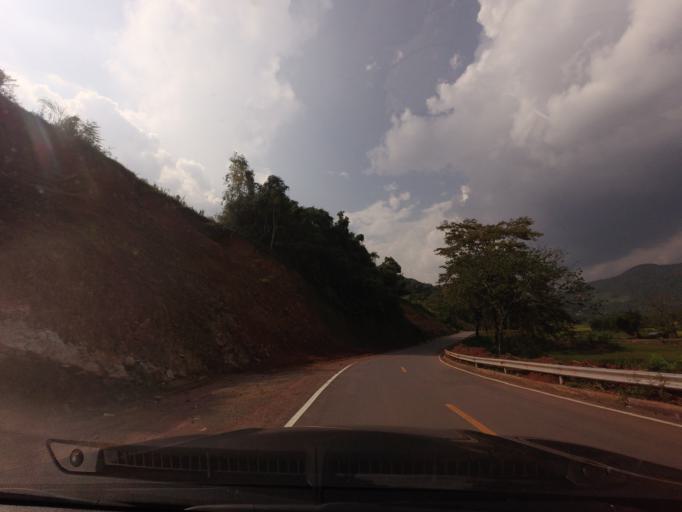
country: TH
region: Nan
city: Bo Kluea
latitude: 19.2185
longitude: 101.1839
